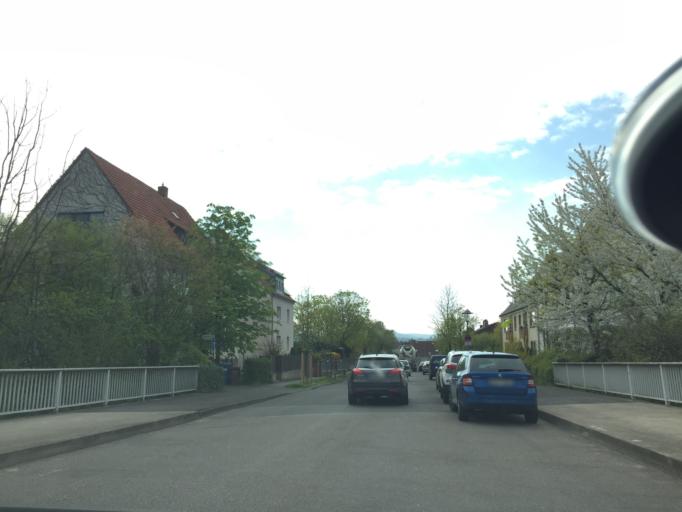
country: DE
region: Bavaria
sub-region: Regierungsbezirk Unterfranken
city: Aschaffenburg
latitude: 49.9834
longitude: 9.1275
